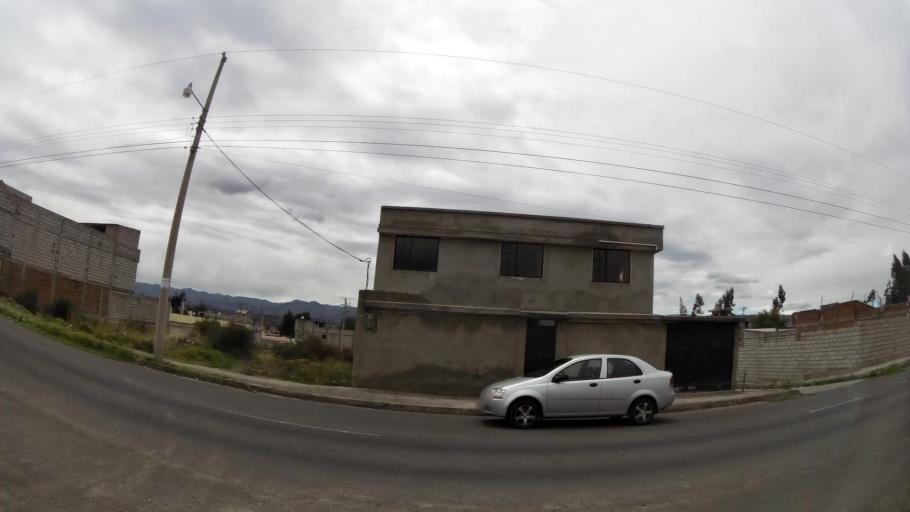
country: EC
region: Cotopaxi
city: Latacunga
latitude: -0.9500
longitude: -78.6022
